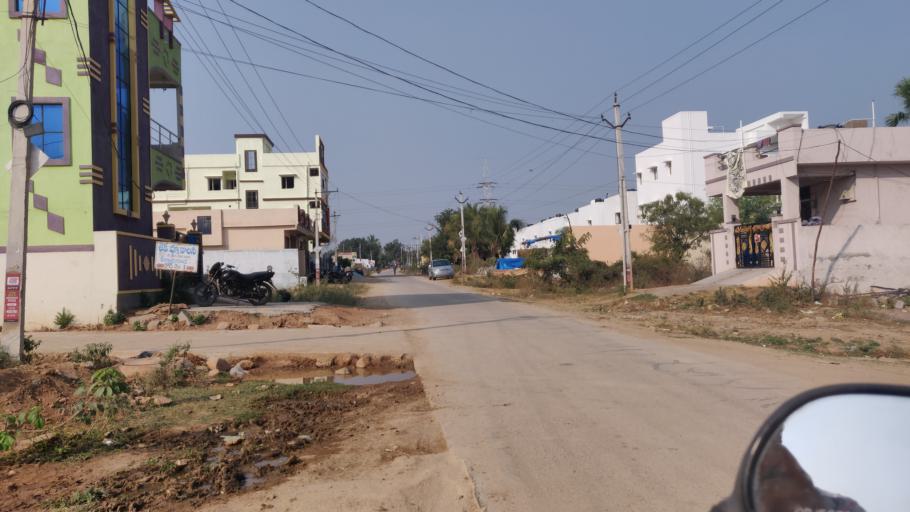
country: IN
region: Telangana
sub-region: Rangareddi
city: Uppal Kalan
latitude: 17.3953
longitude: 78.6050
